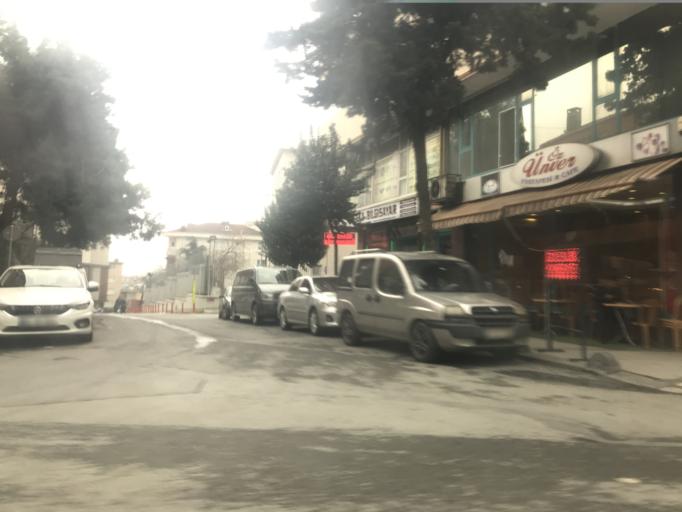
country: TR
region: Istanbul
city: Mahmutbey
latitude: 41.0355
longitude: 28.8339
